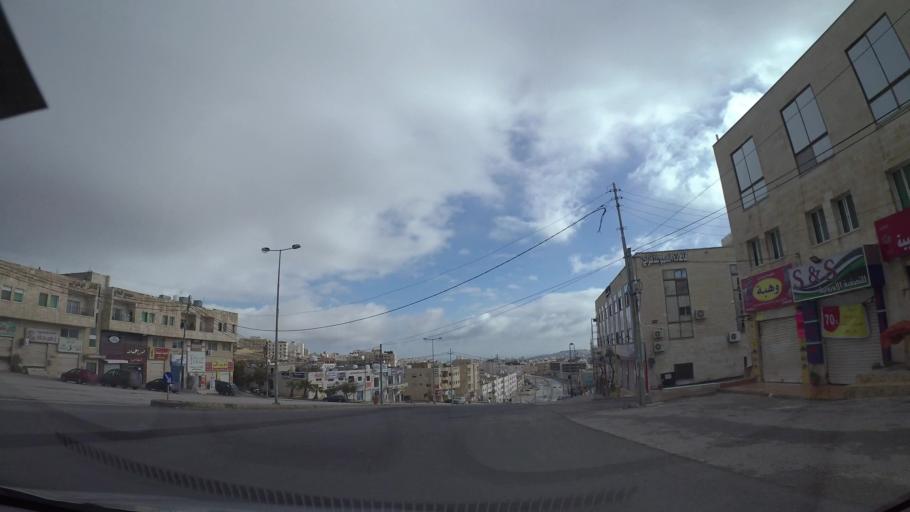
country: JO
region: Amman
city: Al Jubayhah
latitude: 32.0533
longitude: 35.8866
